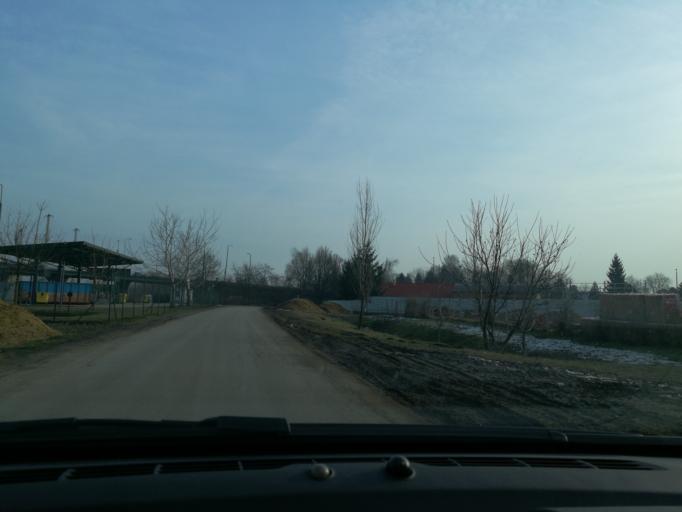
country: HU
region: Szabolcs-Szatmar-Bereg
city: Nyiregyhaza
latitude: 47.9587
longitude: 21.6941
